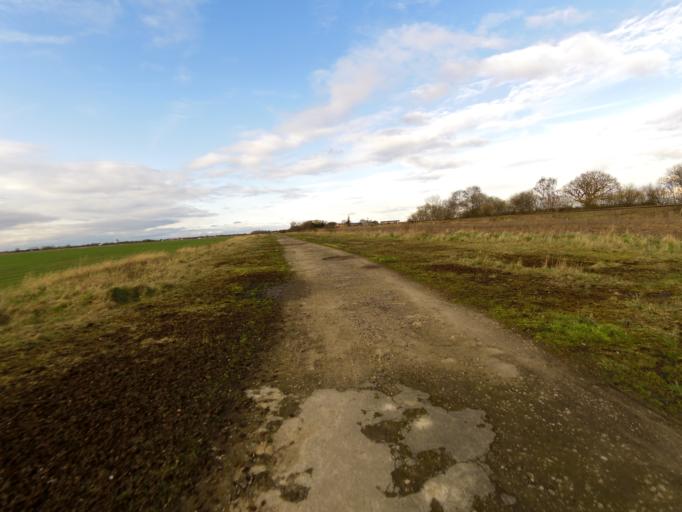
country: GB
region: England
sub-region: North Yorkshire
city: Brayton
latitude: 53.7381
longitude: -1.0827
